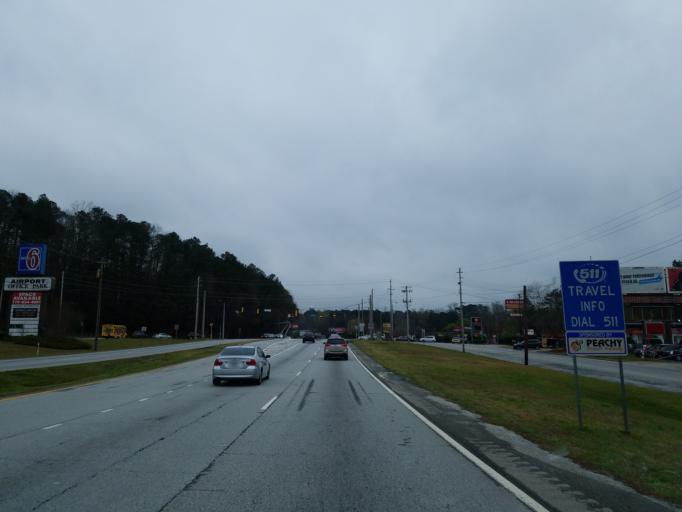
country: US
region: Georgia
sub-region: Fulton County
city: College Park
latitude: 33.6552
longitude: -84.4940
